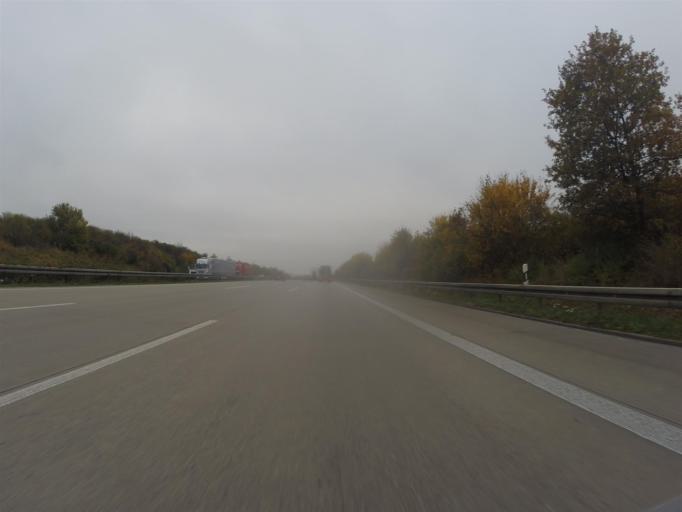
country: DE
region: Thuringia
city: Walpernhain
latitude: 51.0109
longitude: 11.9252
